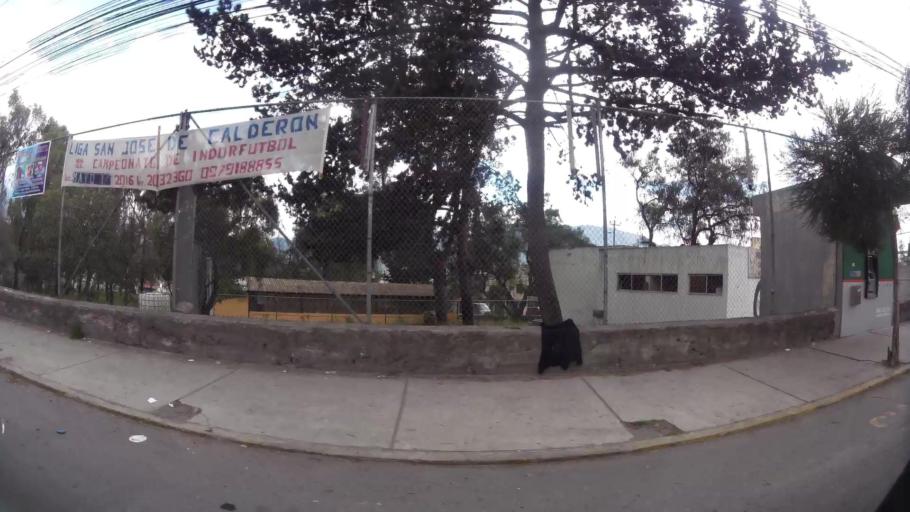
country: EC
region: Pichincha
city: Quito
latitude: -0.0891
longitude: -78.4400
